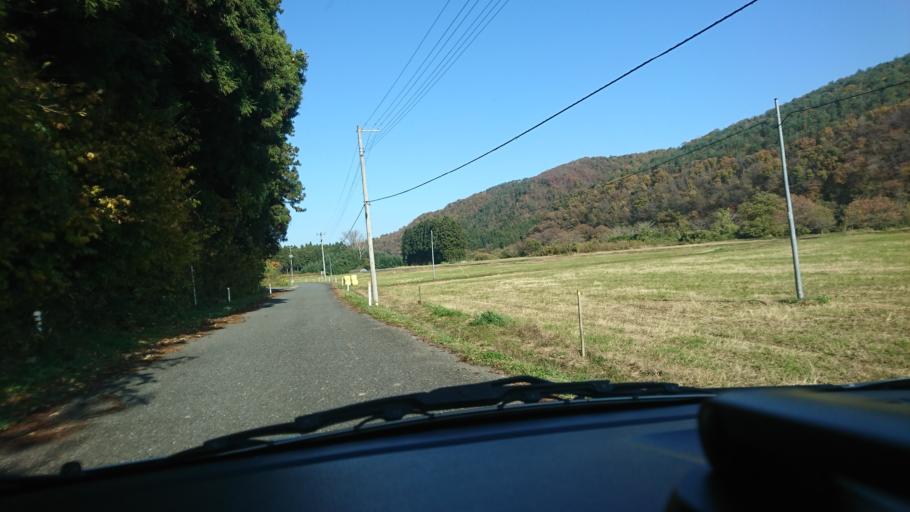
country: JP
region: Iwate
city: Ichinoseki
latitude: 38.8130
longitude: 141.2488
